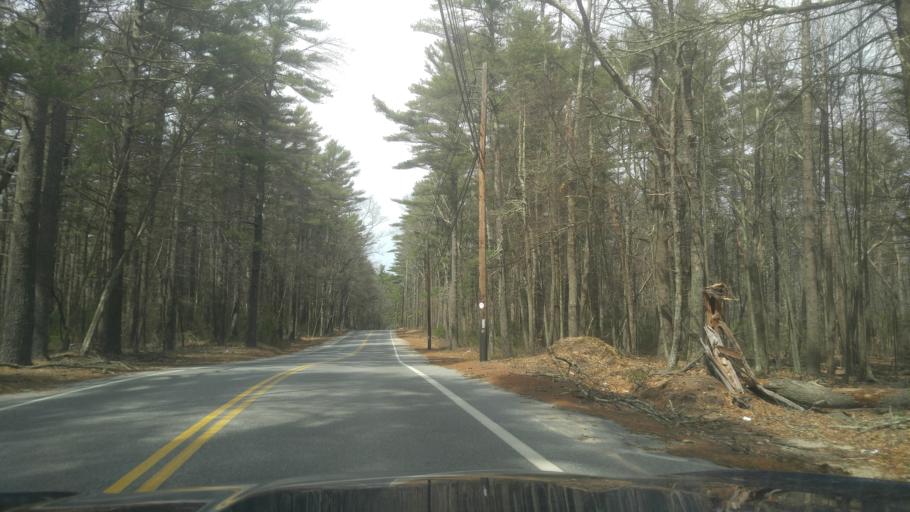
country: US
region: Rhode Island
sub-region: Washington County
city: Exeter
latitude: 41.6332
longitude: -71.5728
